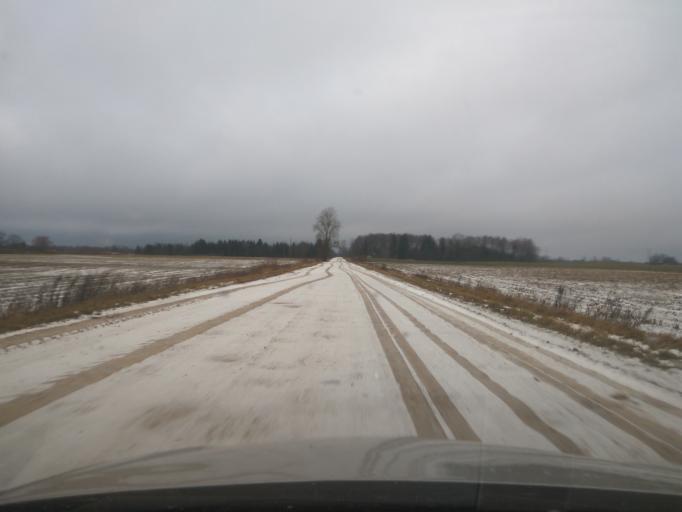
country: LV
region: Saldus Rajons
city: Saldus
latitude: 56.8096
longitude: 22.3083
